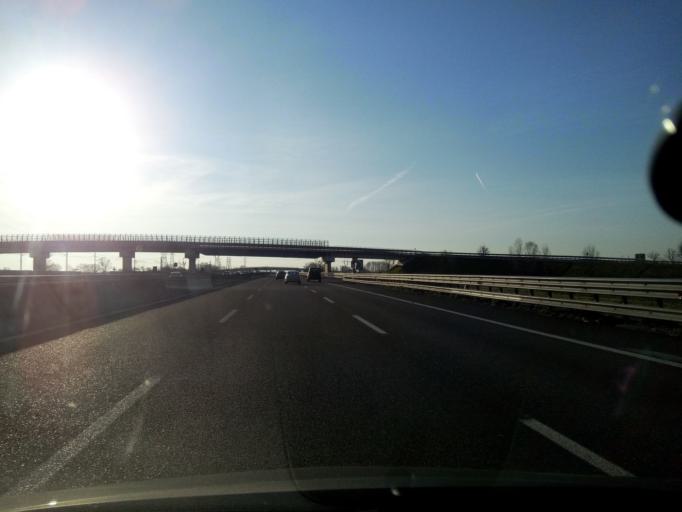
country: IT
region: Emilia-Romagna
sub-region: Provincia di Piacenza
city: Roveleto
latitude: 44.9905
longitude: 9.8393
